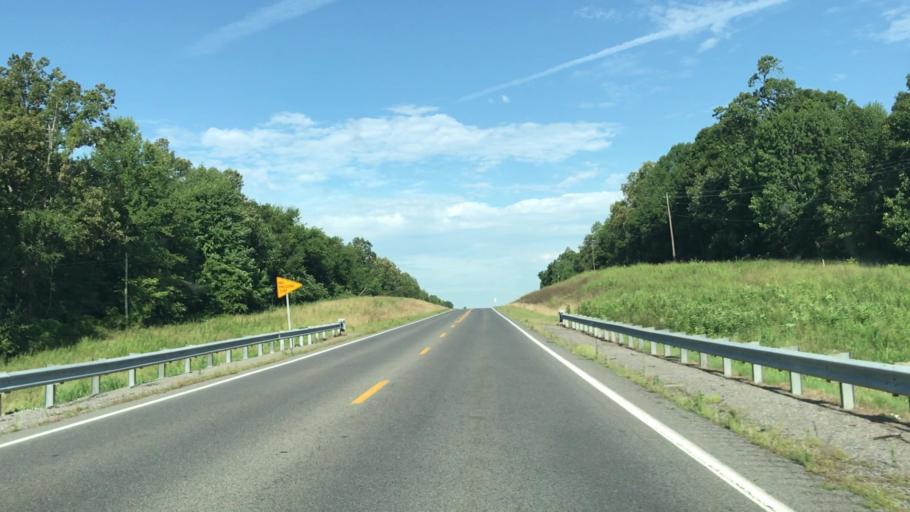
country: US
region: Kentucky
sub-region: Marshall County
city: Calvert City
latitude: 37.0051
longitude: -88.3961
